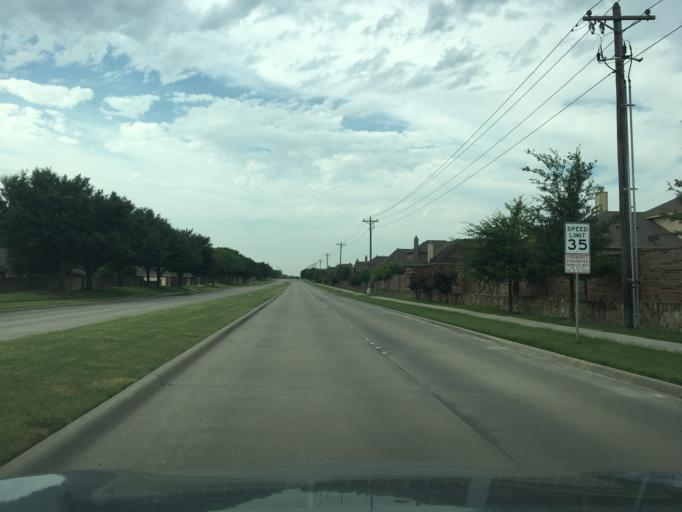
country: US
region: Texas
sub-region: Collin County
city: Murphy
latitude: 33.0399
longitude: -96.5947
